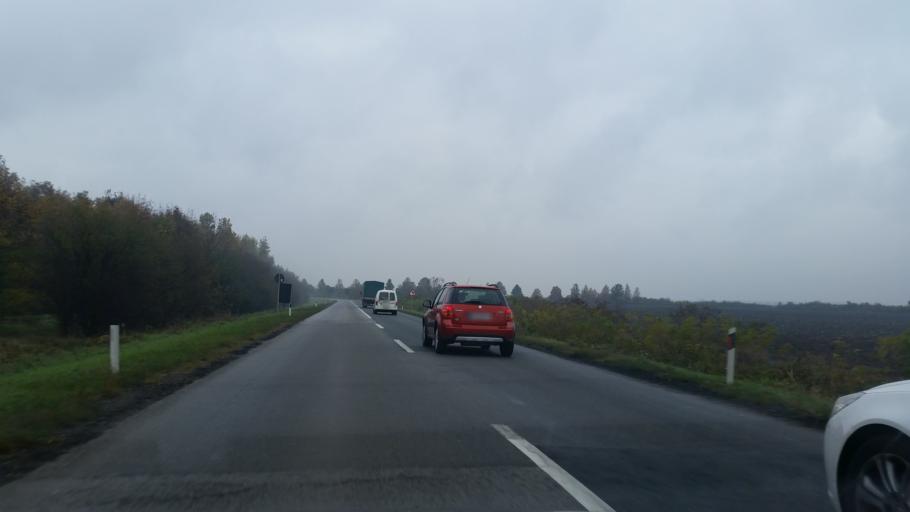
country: RS
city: Sefkerin
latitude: 44.9486
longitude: 20.4327
